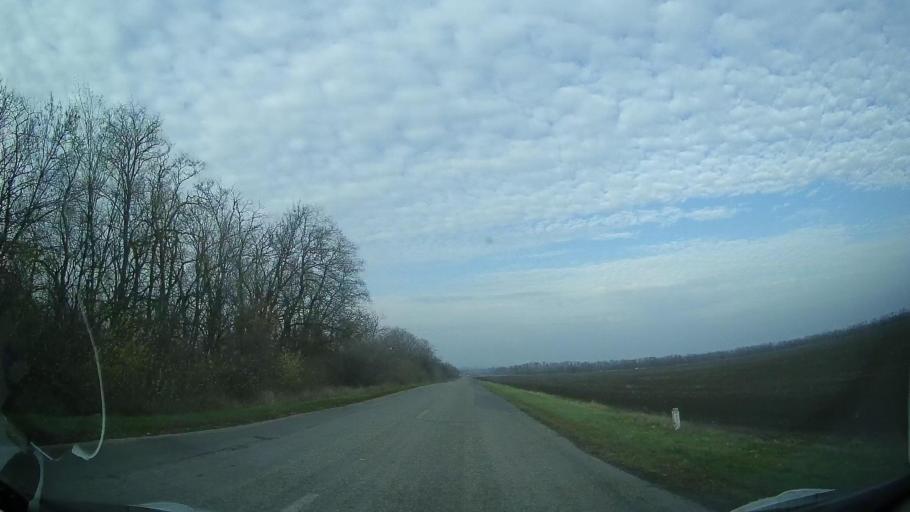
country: RU
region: Rostov
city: Bagayevskaya
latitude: 47.0857
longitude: 40.3915
